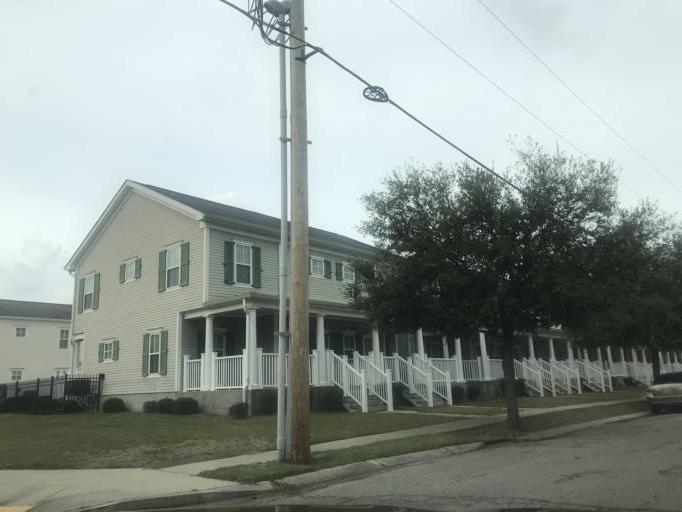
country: US
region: Louisiana
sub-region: Orleans Parish
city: New Orleans
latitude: 29.9487
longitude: -90.0907
